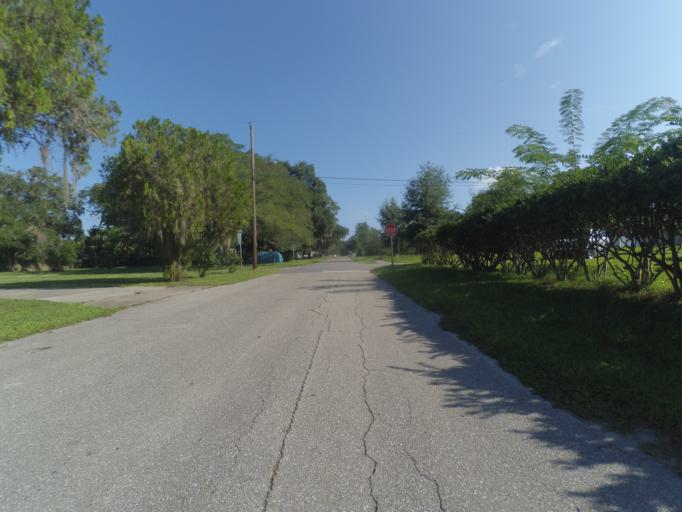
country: US
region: Florida
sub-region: Lake County
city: Umatilla
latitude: 28.9345
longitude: -81.6694
